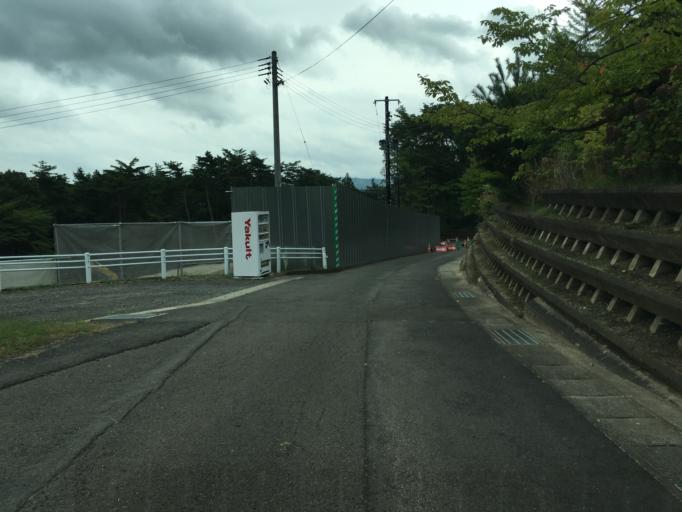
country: JP
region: Fukushima
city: Fukushima-shi
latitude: 37.7761
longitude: 140.4792
